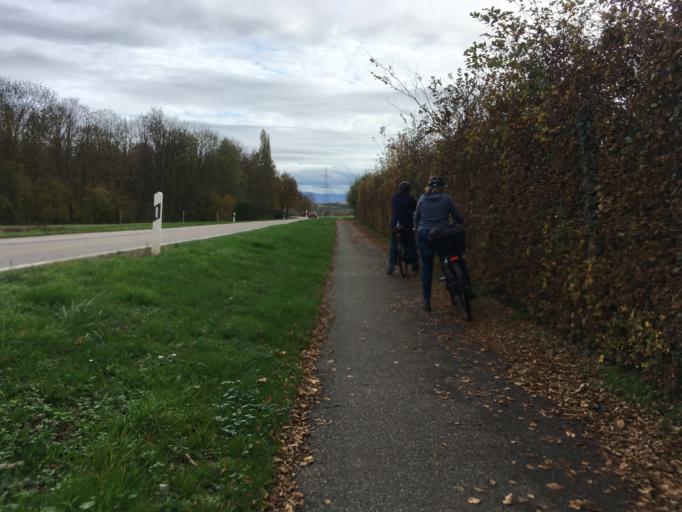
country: DE
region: Baden-Wuerttemberg
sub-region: Freiburg Region
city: Ihringen
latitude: 48.0300
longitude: 7.6604
